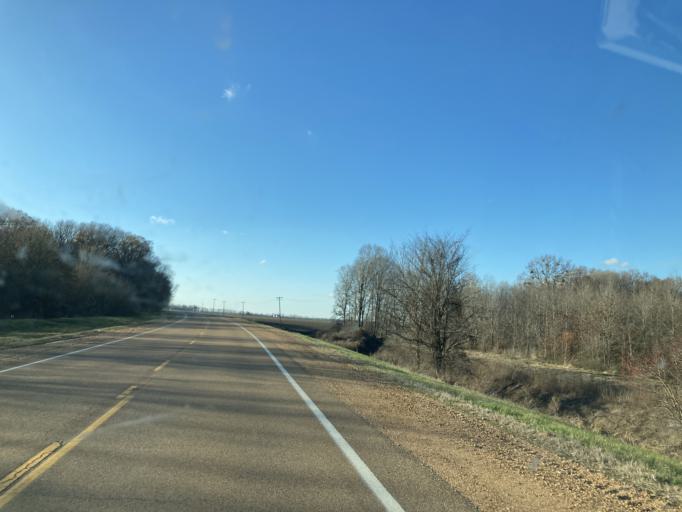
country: US
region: Mississippi
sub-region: Yazoo County
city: Yazoo City
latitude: 32.9240
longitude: -90.5692
